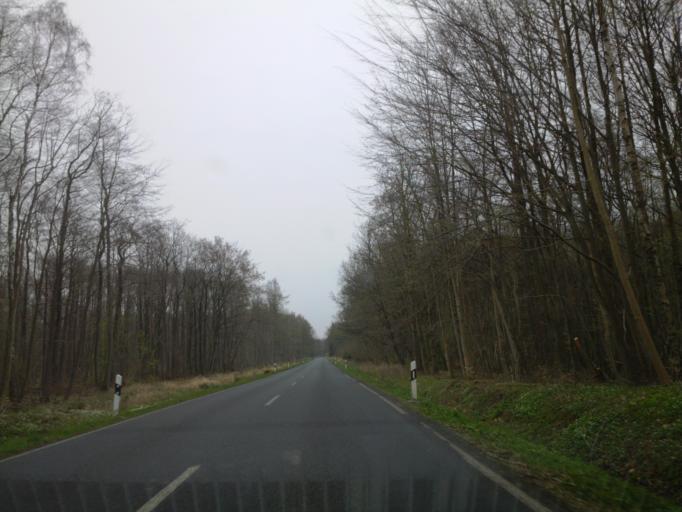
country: DE
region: Mecklenburg-Vorpommern
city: Velgast
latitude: 54.2373
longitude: 12.7255
